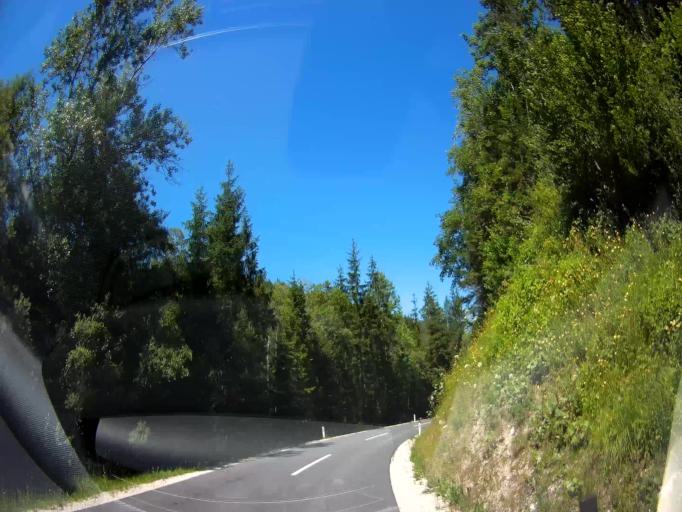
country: AT
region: Carinthia
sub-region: Politischer Bezirk Klagenfurt Land
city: Ferlach
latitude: 46.5106
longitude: 14.2916
